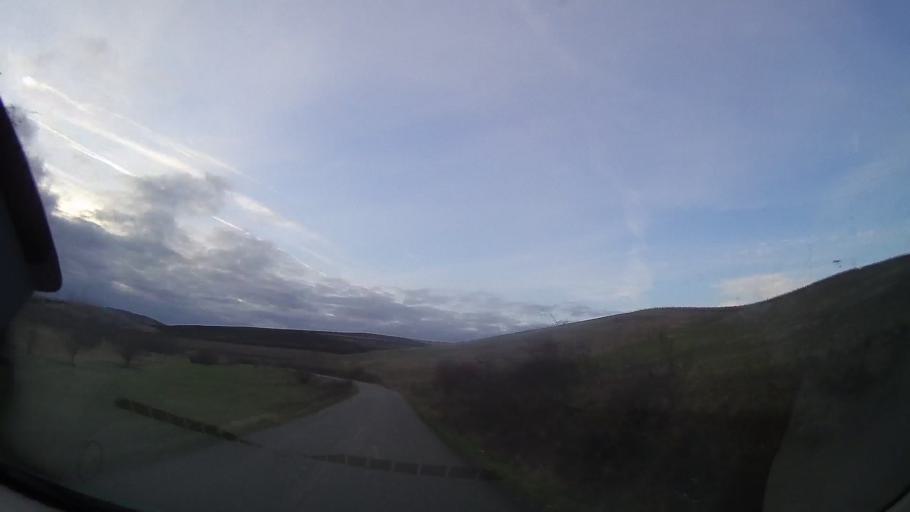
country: RO
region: Cluj
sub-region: Comuna Geaca
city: Geaca
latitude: 46.8532
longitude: 24.0706
